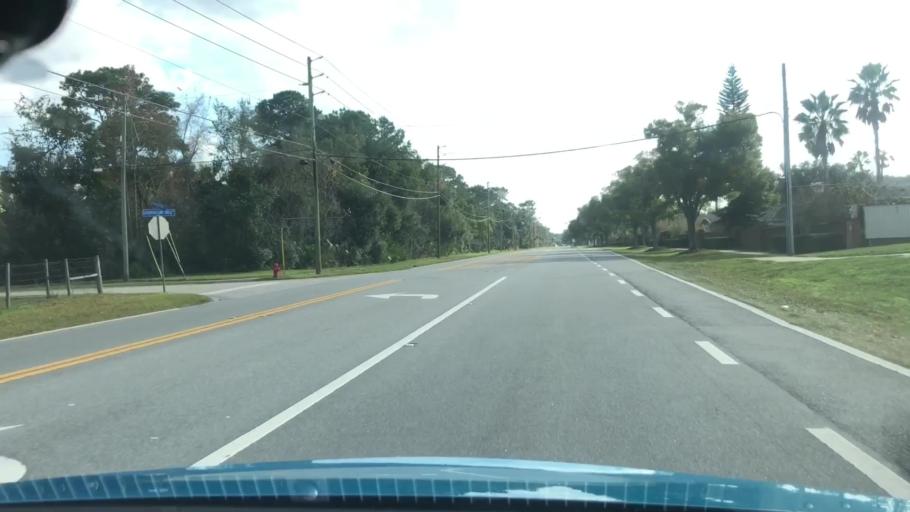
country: US
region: Florida
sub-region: Seminole County
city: Lake Mary
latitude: 28.7419
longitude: -81.3344
